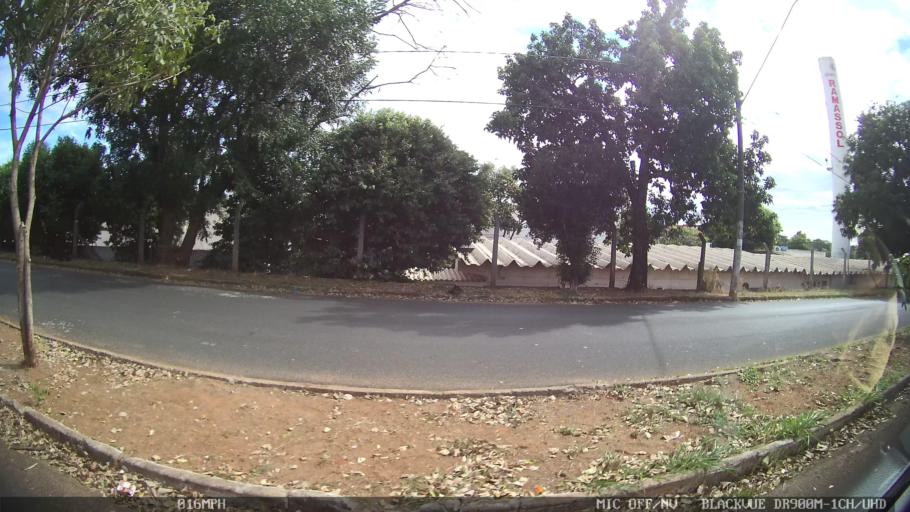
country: BR
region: Sao Paulo
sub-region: Bady Bassitt
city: Bady Bassitt
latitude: -20.8077
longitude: -49.5125
